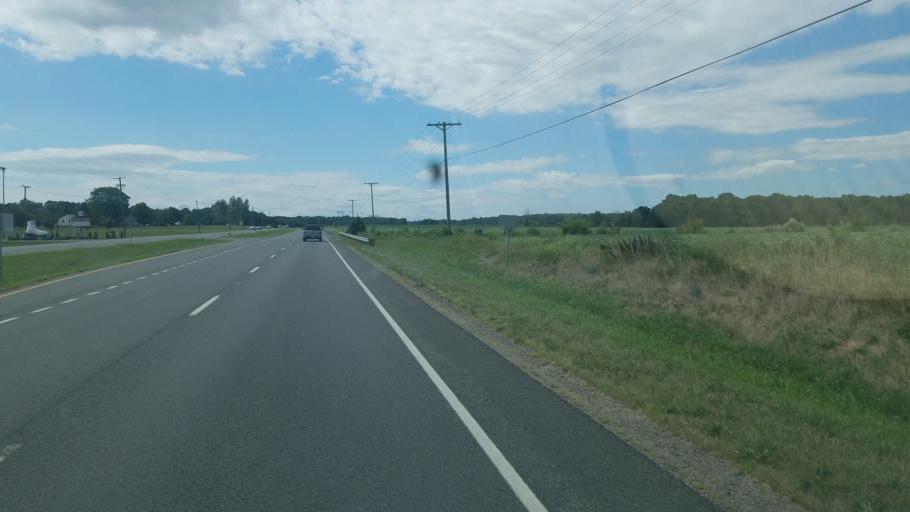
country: US
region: Virginia
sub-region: Fauquier County
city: Bealeton
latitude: 38.5376
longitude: -77.7298
